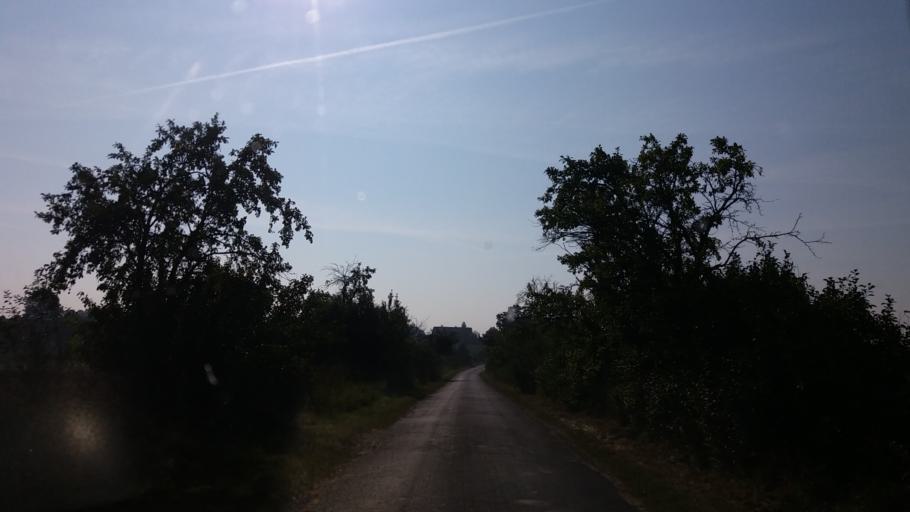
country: PL
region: West Pomeranian Voivodeship
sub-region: Powiat choszczenski
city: Pelczyce
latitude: 53.0181
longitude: 15.3341
